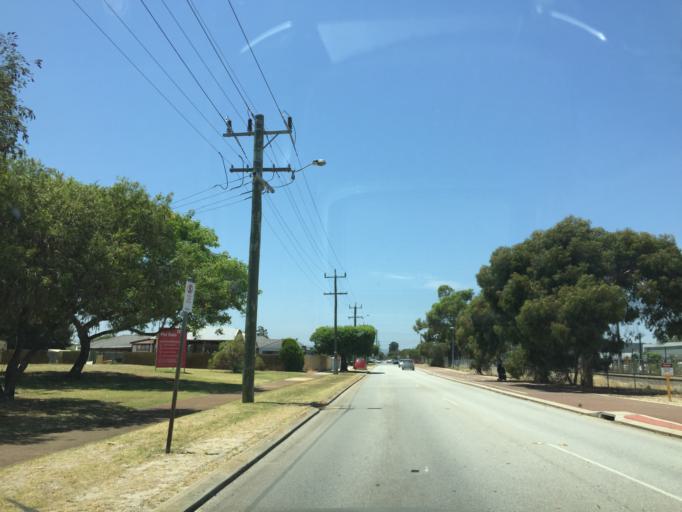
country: AU
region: Western Australia
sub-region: Canning
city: Queens Park
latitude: -32.0079
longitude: 115.9397
